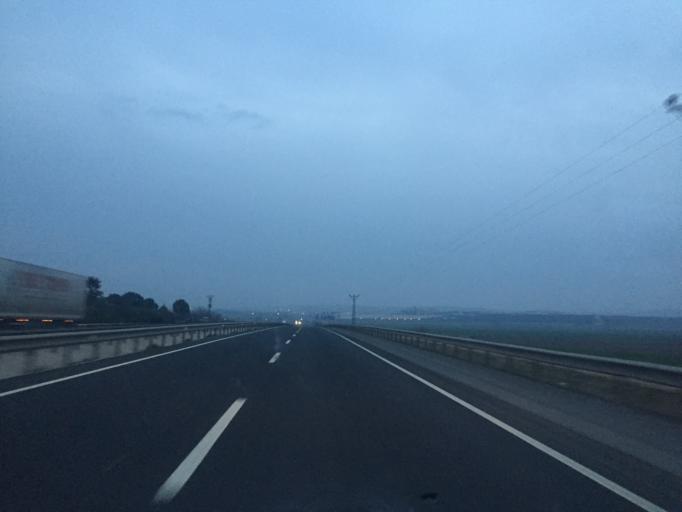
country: TR
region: Sanliurfa
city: Camlidere
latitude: 37.1525
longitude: 39.0742
